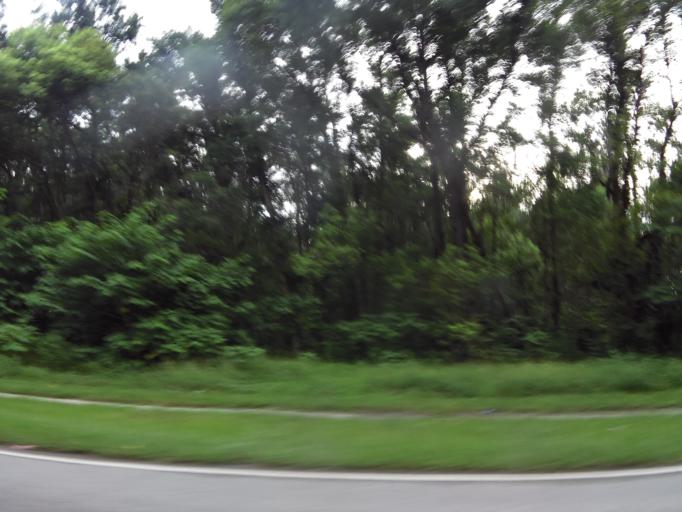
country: US
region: Florida
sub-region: Duval County
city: Jacksonville
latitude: 30.3831
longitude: -81.6990
